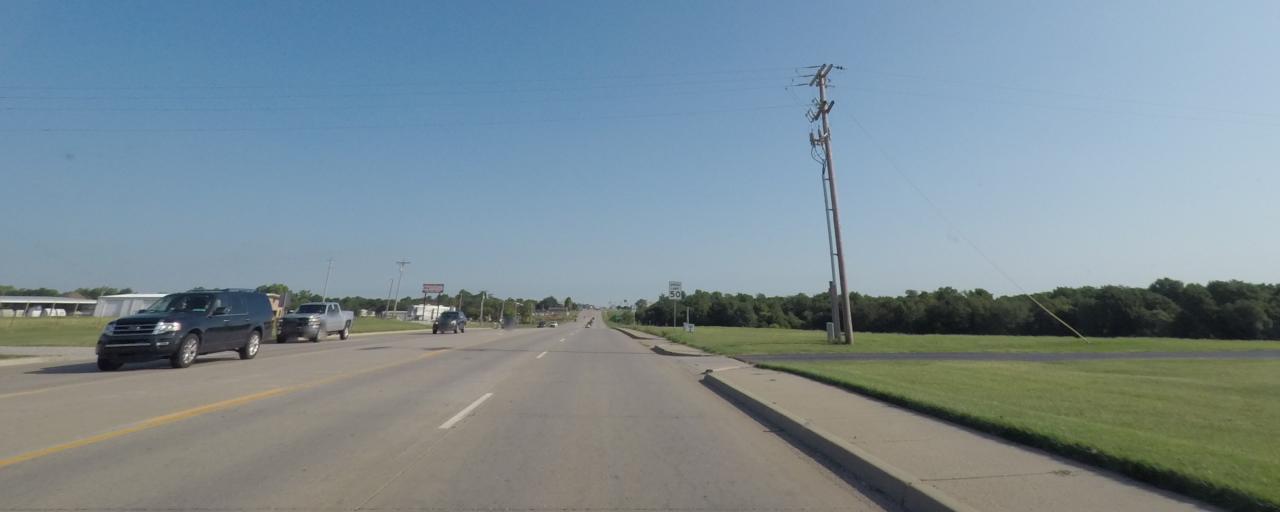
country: US
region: Oklahoma
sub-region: McClain County
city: Newcastle
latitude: 35.2636
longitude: -97.6001
